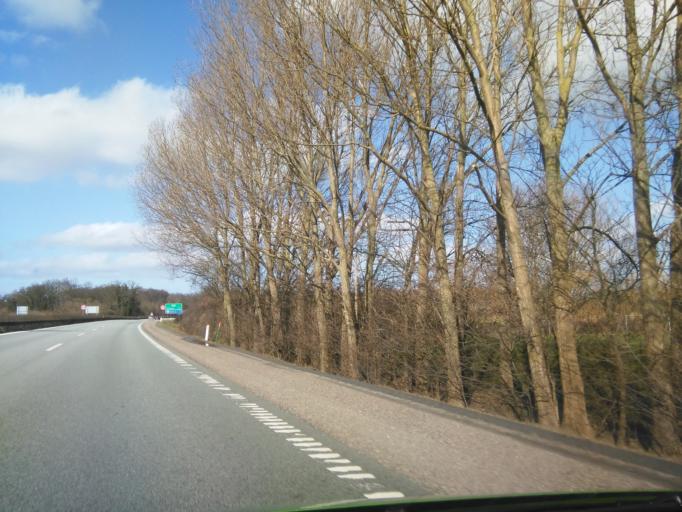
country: DK
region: South Denmark
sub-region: Nyborg Kommune
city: Nyborg
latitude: 55.3136
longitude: 10.8073
